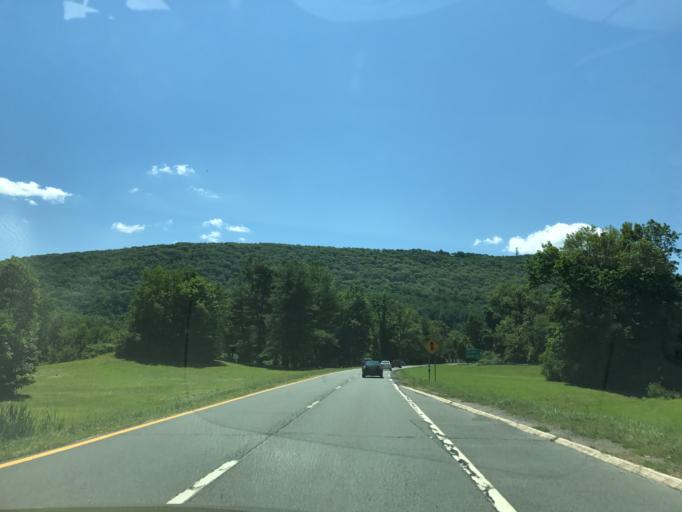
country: US
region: New York
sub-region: Dutchess County
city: Hillside Lake
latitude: 41.5418
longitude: -73.7733
